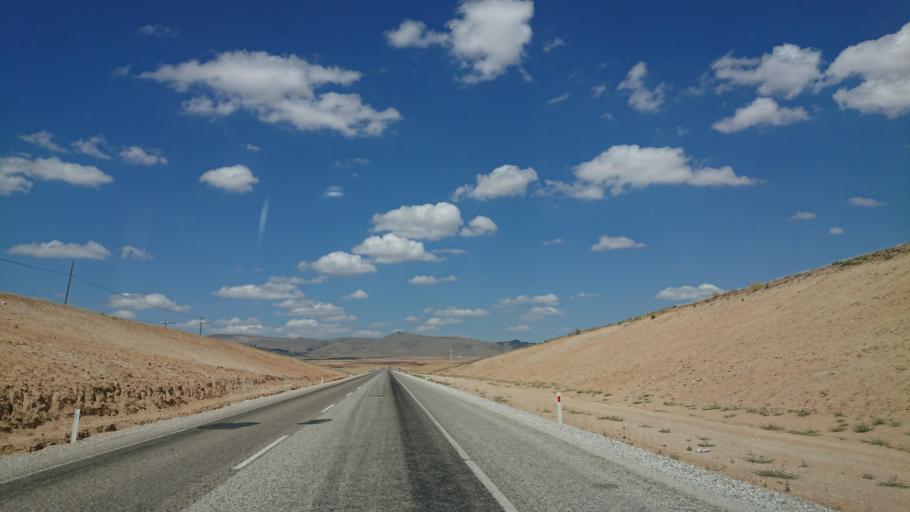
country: TR
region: Ankara
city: Evren
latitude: 39.1154
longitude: 33.9427
